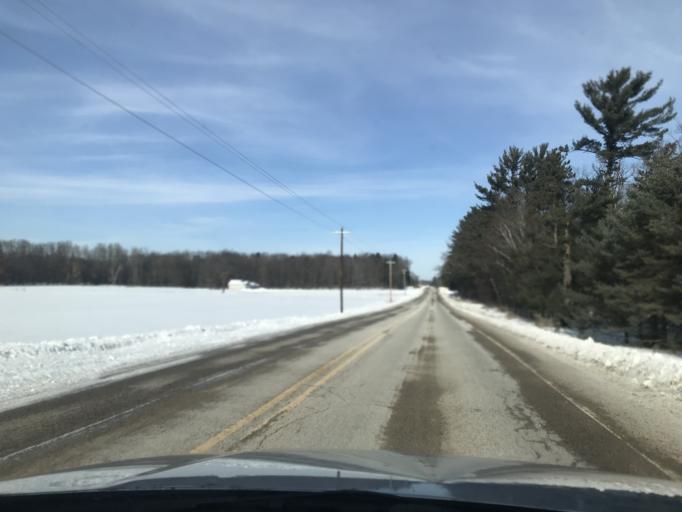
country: US
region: Wisconsin
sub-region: Oconto County
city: Oconto Falls
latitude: 45.1347
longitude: -88.1775
